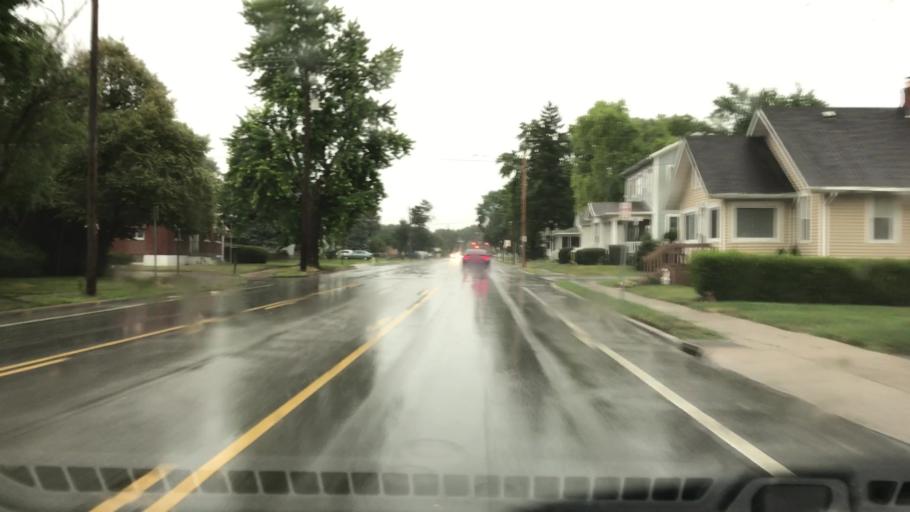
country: US
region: Ohio
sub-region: Greene County
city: Fairborn
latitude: 39.8195
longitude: -84.0249
